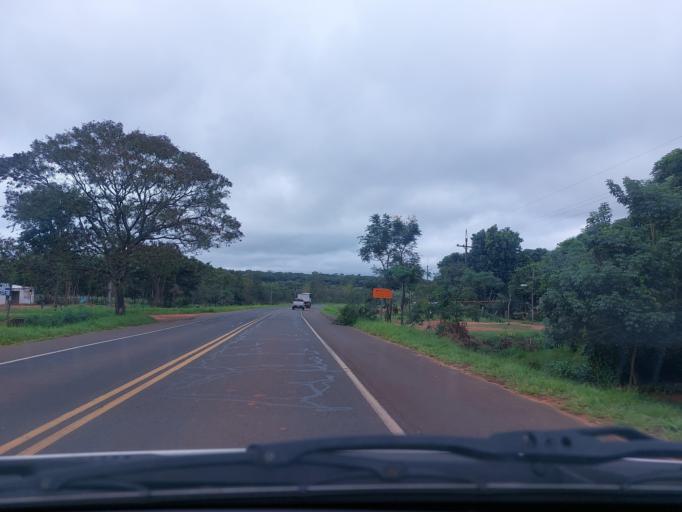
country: PY
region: San Pedro
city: Guayaybi
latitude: -24.6406
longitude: -56.3773
